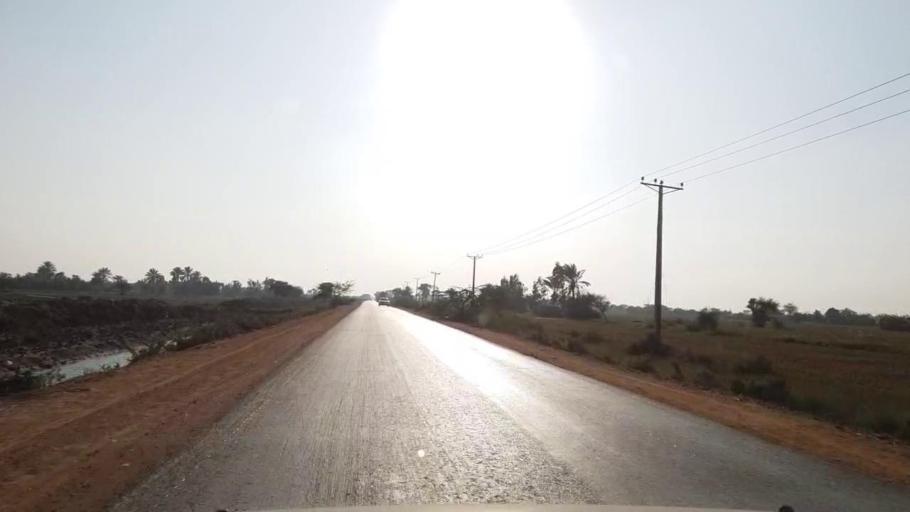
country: PK
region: Sindh
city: Mirpur Batoro
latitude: 24.7939
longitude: 68.3007
